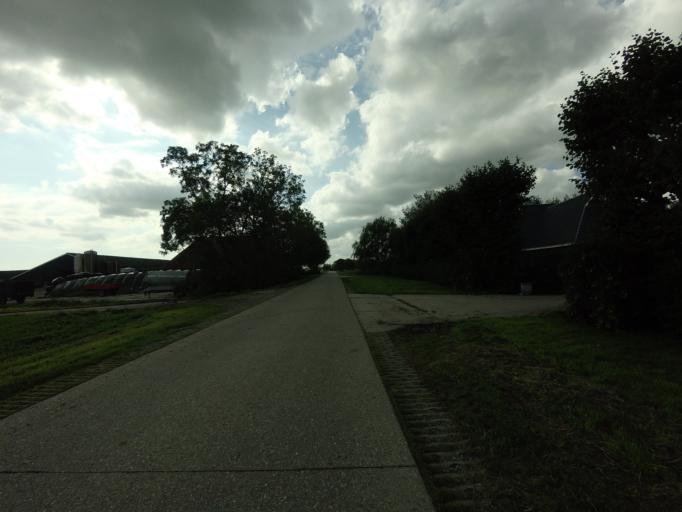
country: NL
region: Friesland
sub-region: Gemeente Littenseradiel
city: Wommels
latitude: 53.0737
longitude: 5.6096
